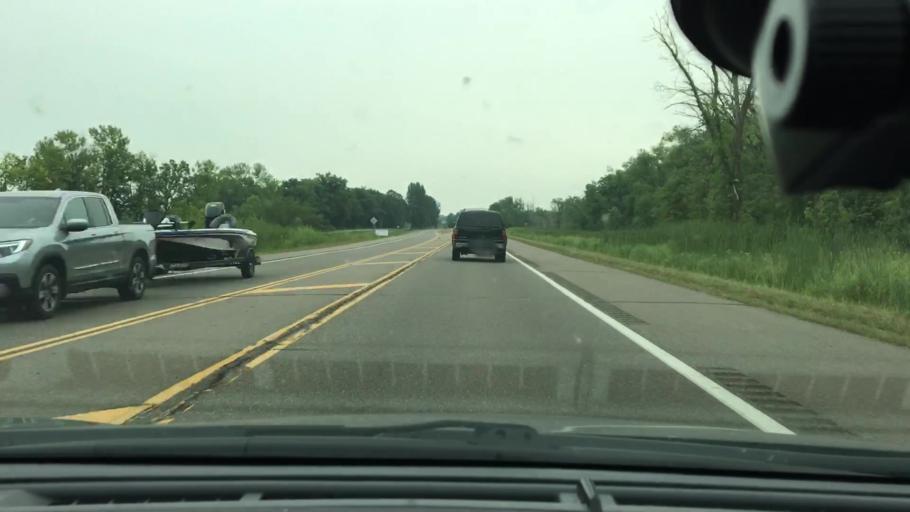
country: US
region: Minnesota
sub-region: Mille Lacs County
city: Vineland
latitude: 46.1975
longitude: -93.7645
